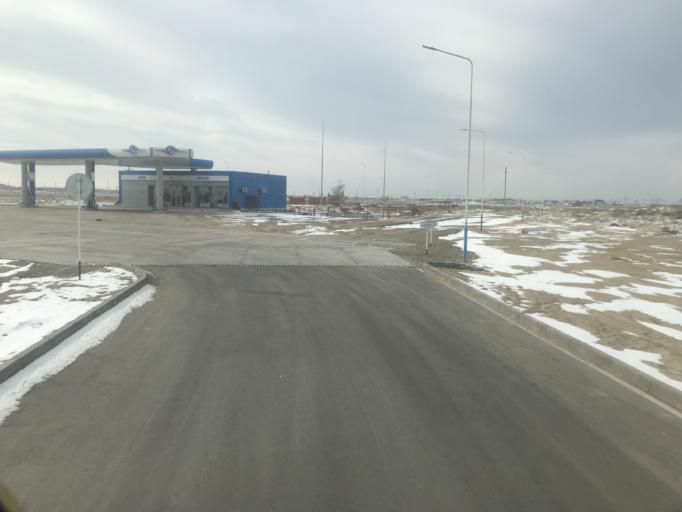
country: KZ
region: Qyzylorda
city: Ayteke Bi
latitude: 45.8765
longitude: 62.1480
